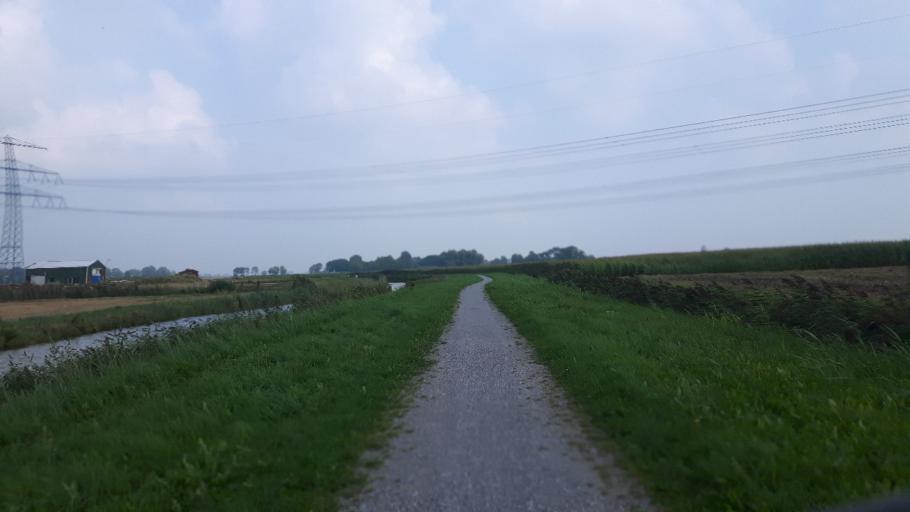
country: NL
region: Groningen
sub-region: Gemeente Bedum
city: Bedum
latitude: 53.3394
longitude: 6.7205
